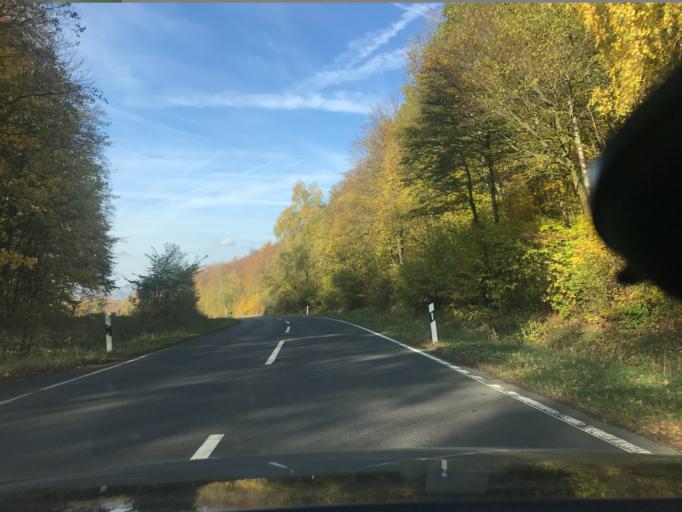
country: DE
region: Hesse
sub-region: Regierungsbezirk Kassel
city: Grossalmerode
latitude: 51.2130
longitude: 9.8274
